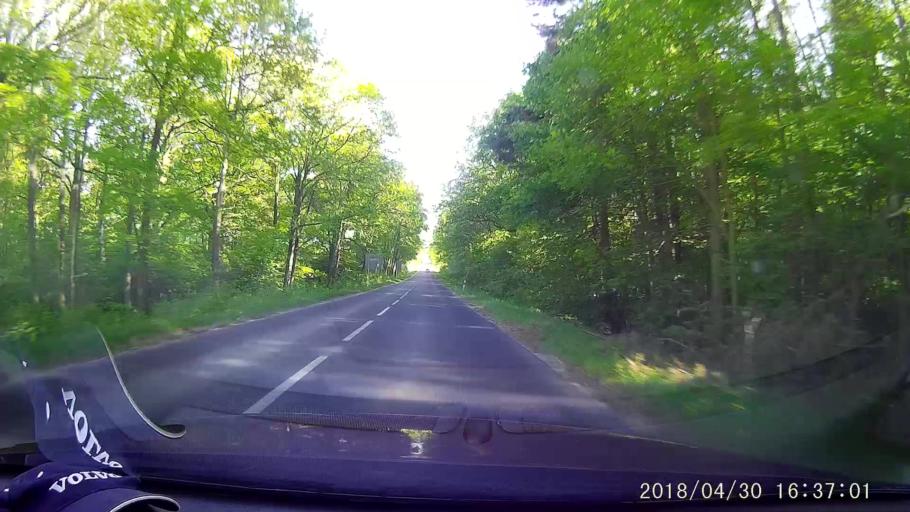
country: PL
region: Lower Silesian Voivodeship
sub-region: Powiat zgorzelecki
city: Sulikow
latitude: 51.0687
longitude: 15.0320
